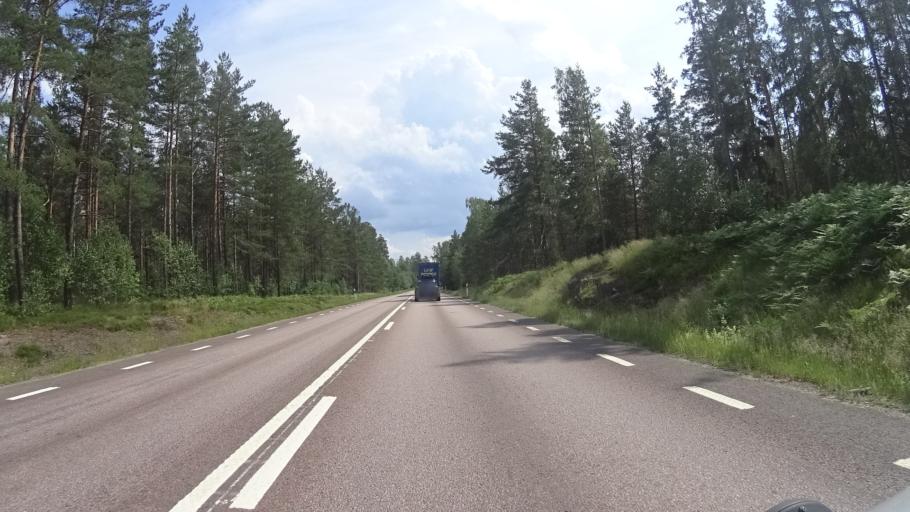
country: SE
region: Kalmar
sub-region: Hultsfreds Kommun
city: Hultsfred
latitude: 57.4781
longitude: 15.8359
